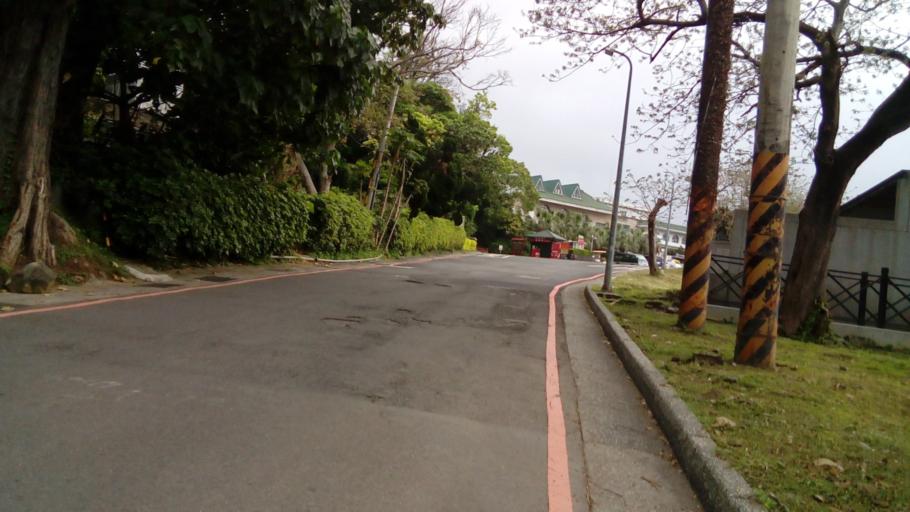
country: TW
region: Taipei
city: Taipei
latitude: 25.1781
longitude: 121.4292
